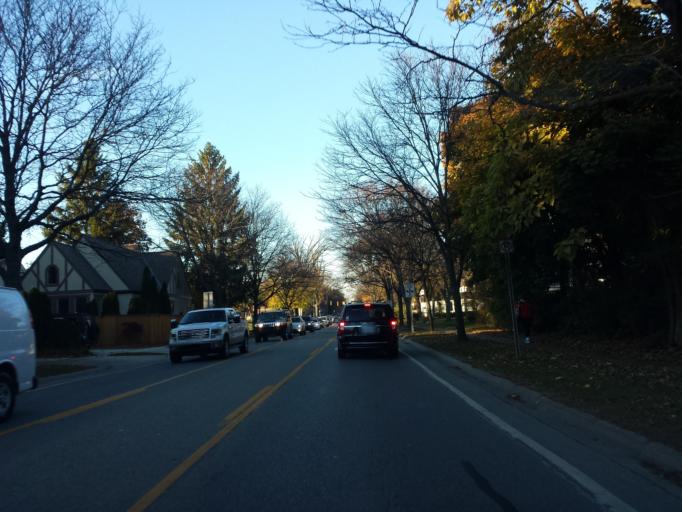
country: US
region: Michigan
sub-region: Oakland County
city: Birmingham
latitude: 42.5482
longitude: -83.2058
